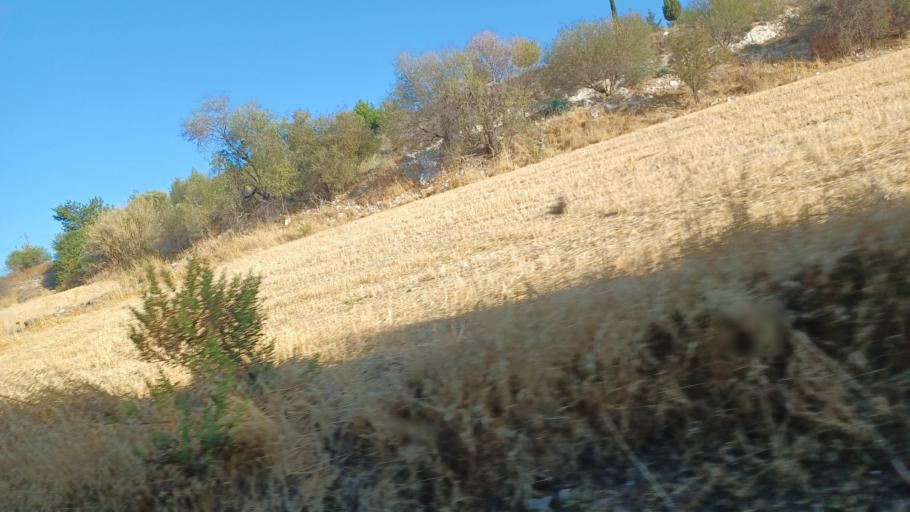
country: CY
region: Pafos
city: Mesogi
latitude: 34.9171
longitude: 32.5326
